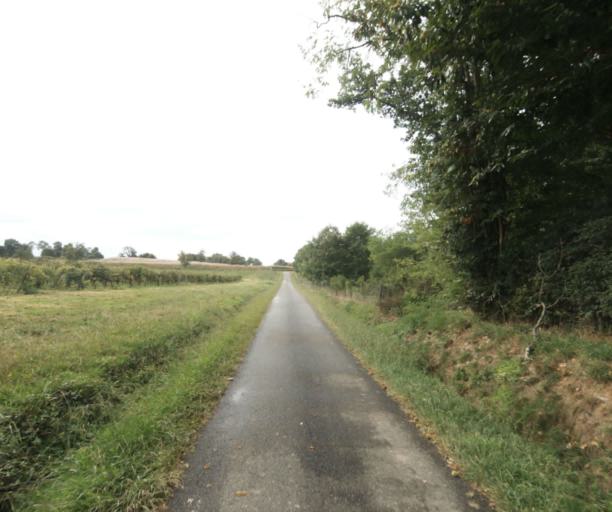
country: FR
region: Midi-Pyrenees
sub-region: Departement du Gers
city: Cazaubon
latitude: 43.9020
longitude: -0.1255
